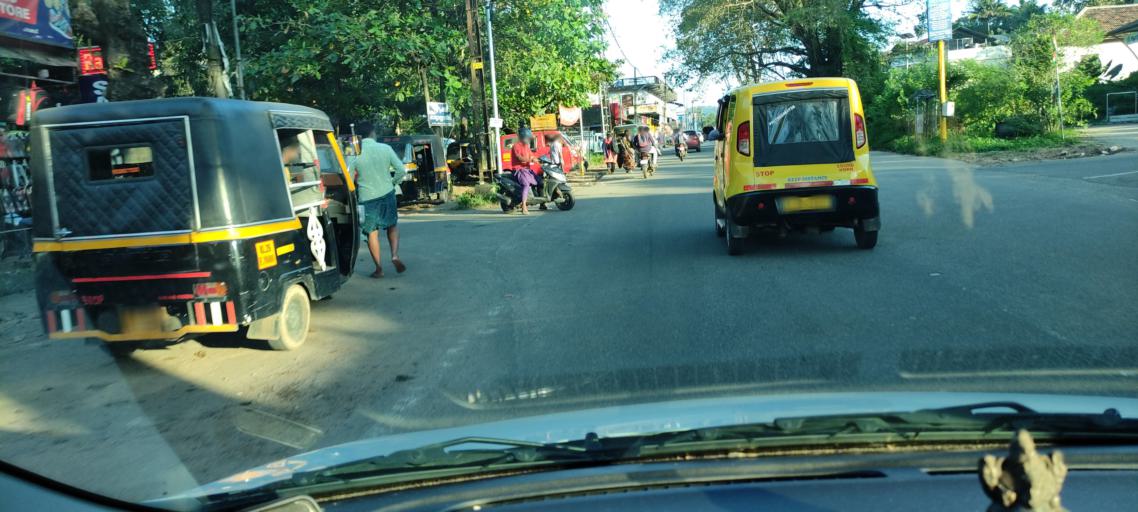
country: IN
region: Kerala
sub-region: Pattanamtitta
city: Adur
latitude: 9.1482
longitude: 76.7607
